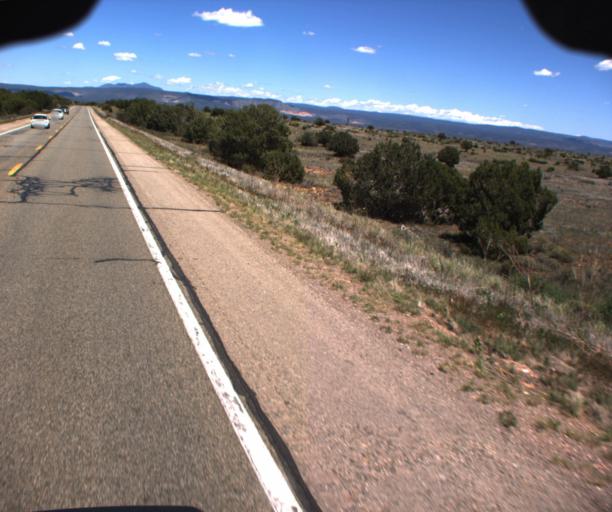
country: US
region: Arizona
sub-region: Yavapai County
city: Paulden
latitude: 34.9527
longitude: -112.4206
